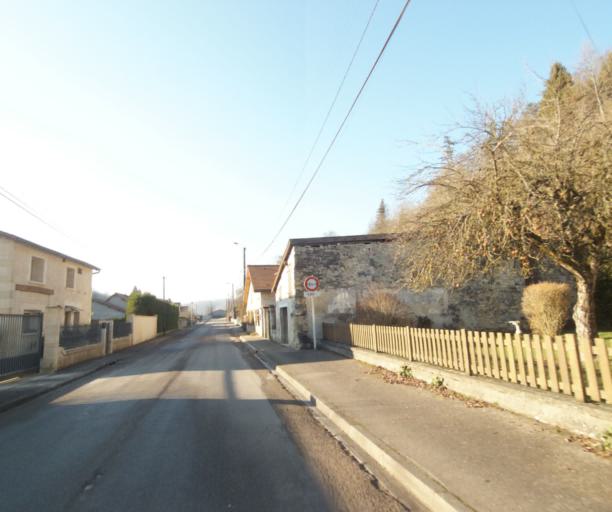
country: FR
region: Champagne-Ardenne
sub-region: Departement de la Haute-Marne
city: Chevillon
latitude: 48.5272
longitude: 5.1470
